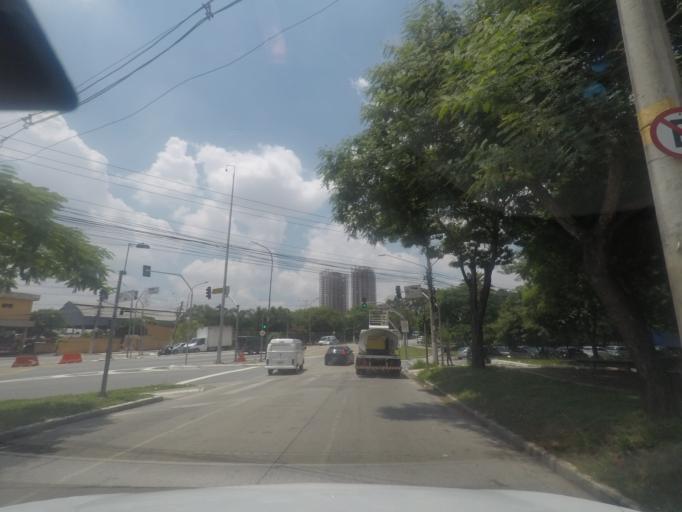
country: BR
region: Sao Paulo
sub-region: Sao Paulo
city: Sao Paulo
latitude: -23.5124
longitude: -46.6667
